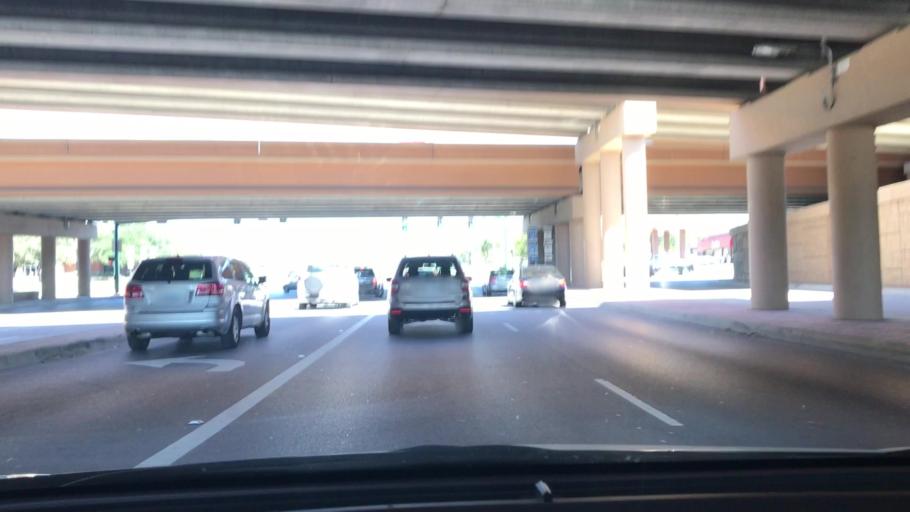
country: US
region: Texas
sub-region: Tarrant County
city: Hurst
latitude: 32.8391
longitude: -97.1862
